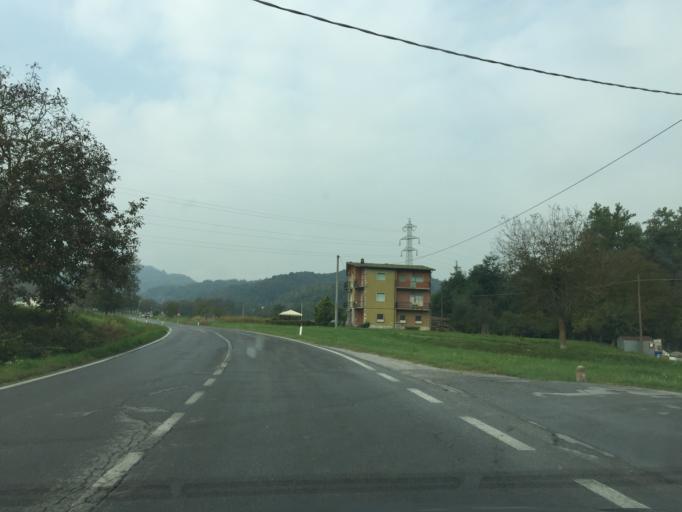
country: IT
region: Piedmont
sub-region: Provincia di Cuneo
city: Roccaforte Mondovi
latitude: 44.3154
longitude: 7.7314
